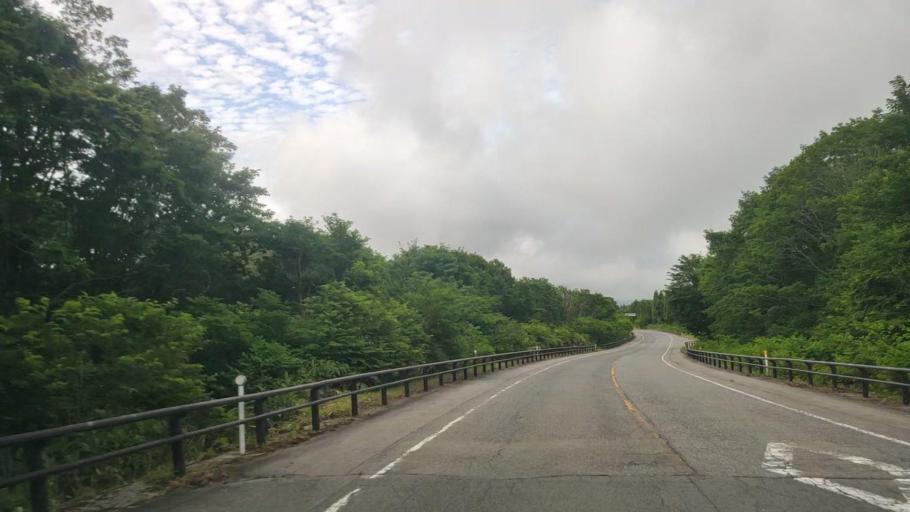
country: JP
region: Tottori
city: Kurayoshi
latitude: 35.3403
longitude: 133.5813
